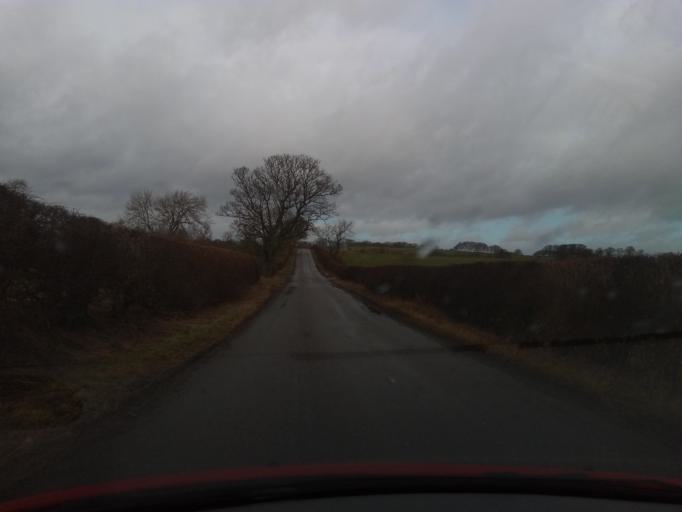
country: GB
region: England
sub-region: Northumberland
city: Rothley
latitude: 55.1838
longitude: -1.9689
